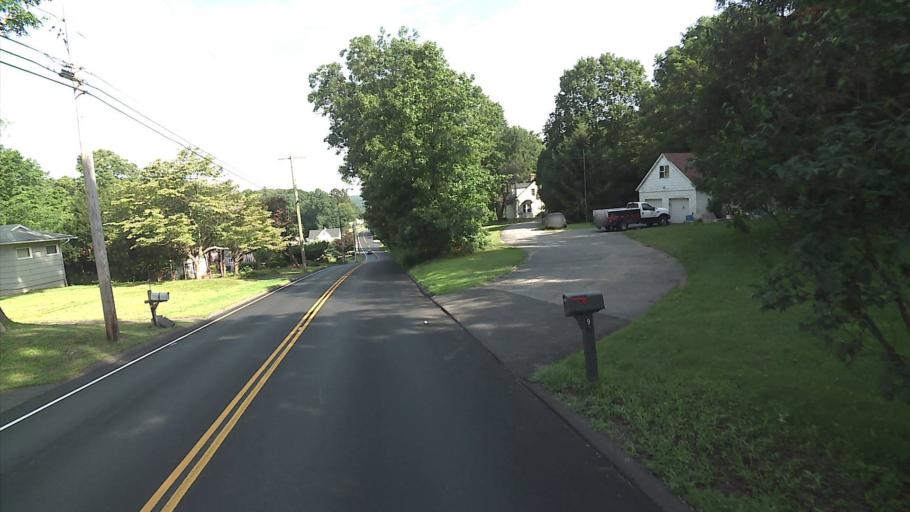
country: US
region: Connecticut
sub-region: New Haven County
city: Seymour
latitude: 41.3830
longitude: -73.0669
